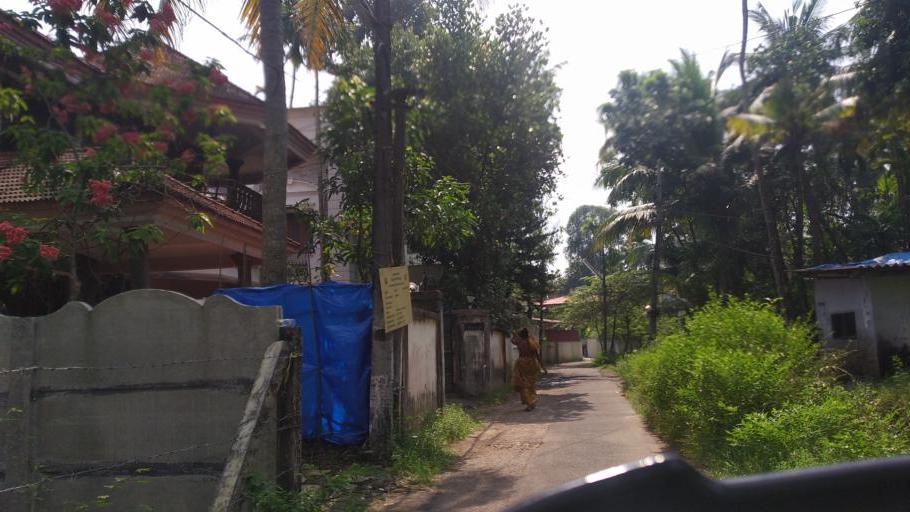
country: IN
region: Kerala
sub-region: Ernakulam
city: Elur
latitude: 10.0594
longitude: 76.2162
